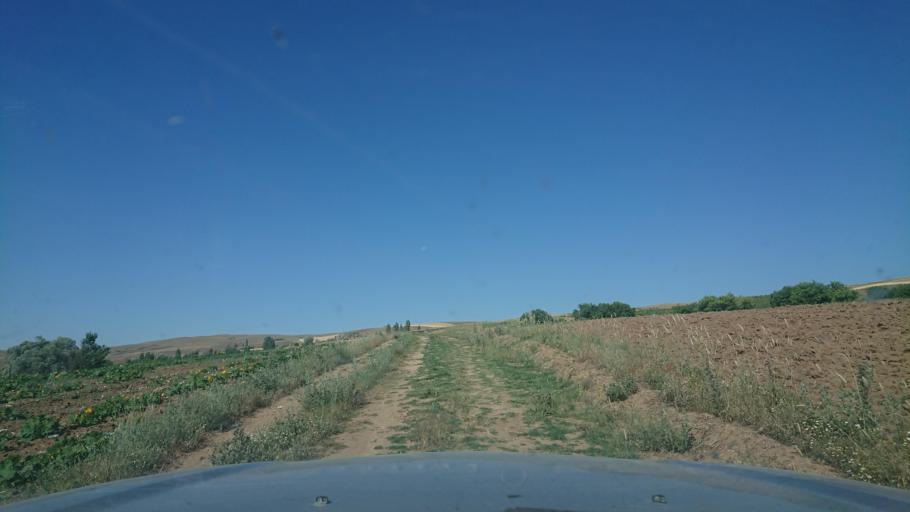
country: TR
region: Aksaray
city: Agacoren
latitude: 38.8477
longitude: 33.9257
